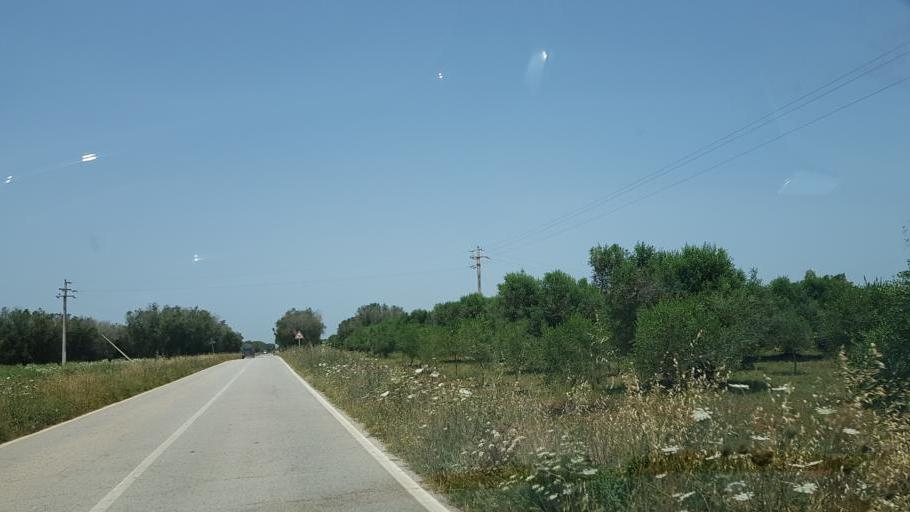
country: IT
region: Apulia
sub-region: Provincia di Brindisi
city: San Pancrazio Salentino
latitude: 40.4528
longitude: 17.8406
